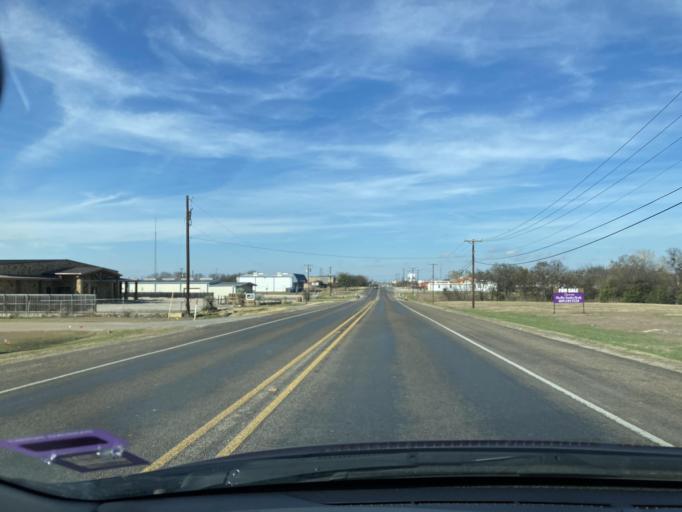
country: US
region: Texas
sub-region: Navarro County
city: Corsicana
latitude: 32.0785
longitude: -96.4483
